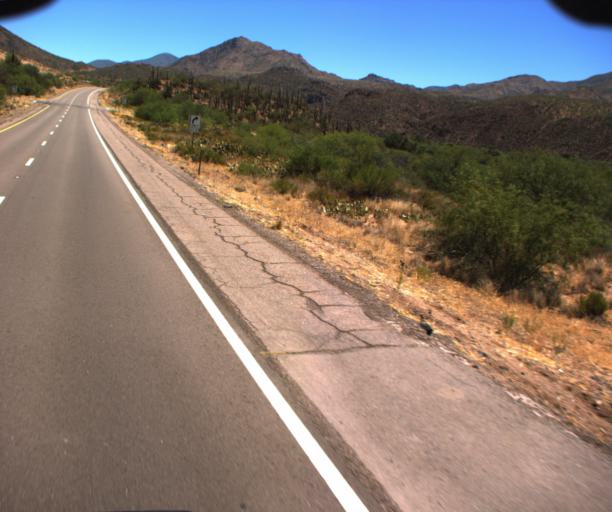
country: US
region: Arizona
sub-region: Maricopa County
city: Rio Verde
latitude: 33.7963
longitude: -111.4923
